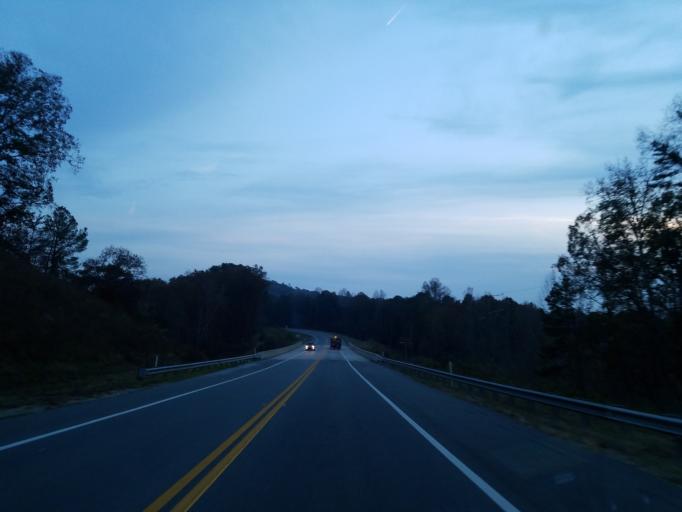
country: US
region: Georgia
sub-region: Pickens County
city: Jasper
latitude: 34.5272
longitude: -84.5709
